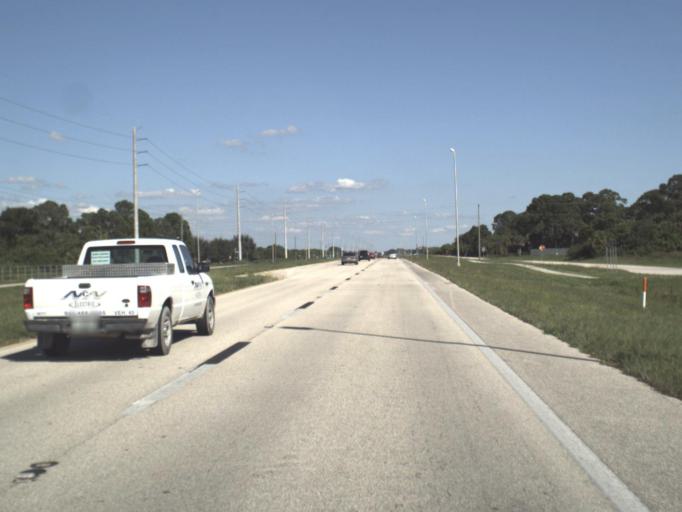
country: US
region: Florida
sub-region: Charlotte County
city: Rotonda
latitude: 26.9326
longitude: -82.2590
